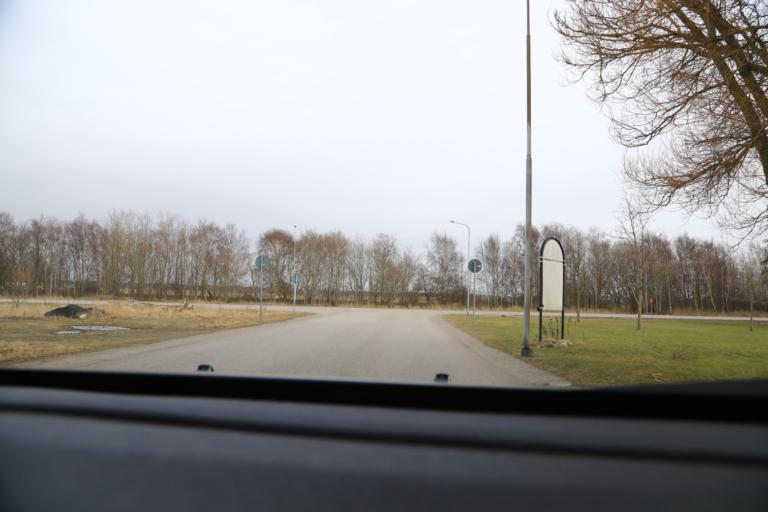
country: SE
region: Halland
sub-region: Kungsbacka Kommun
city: Frillesas
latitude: 57.2384
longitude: 12.1322
